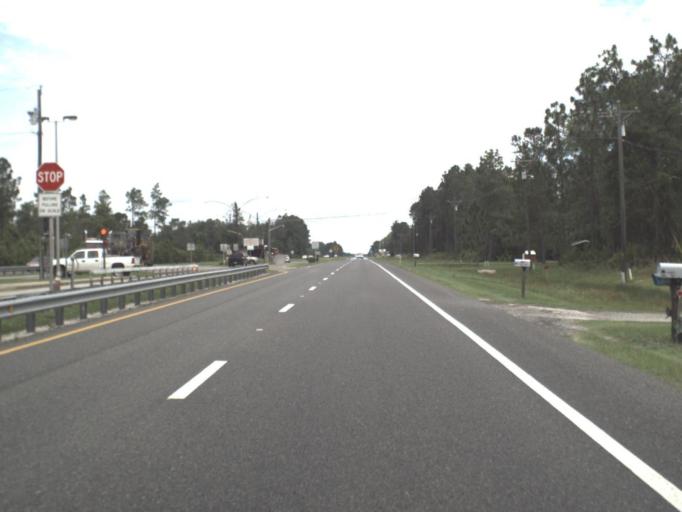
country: US
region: Florida
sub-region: Nassau County
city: Hilliard
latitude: 30.7432
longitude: -81.9540
